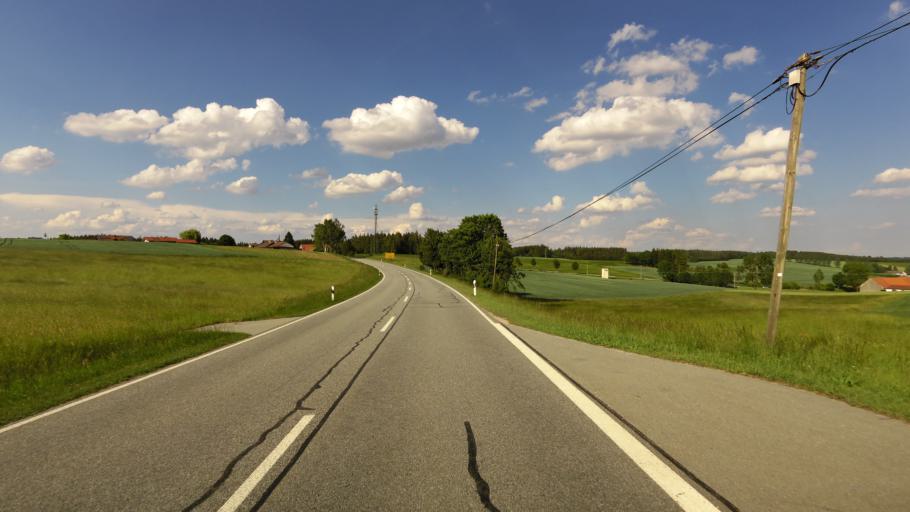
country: DE
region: Bavaria
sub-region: Lower Bavaria
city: Vilsheim
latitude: 48.4266
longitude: 12.1368
